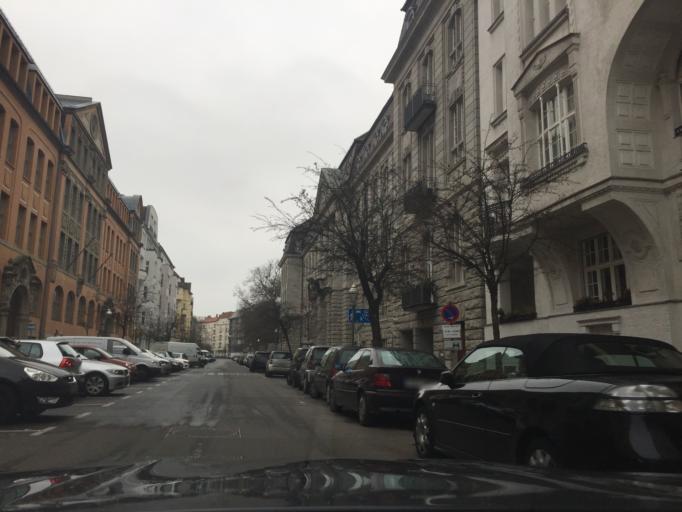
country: DE
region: Berlin
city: Charlottenburg Bezirk
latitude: 52.5099
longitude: 13.2950
